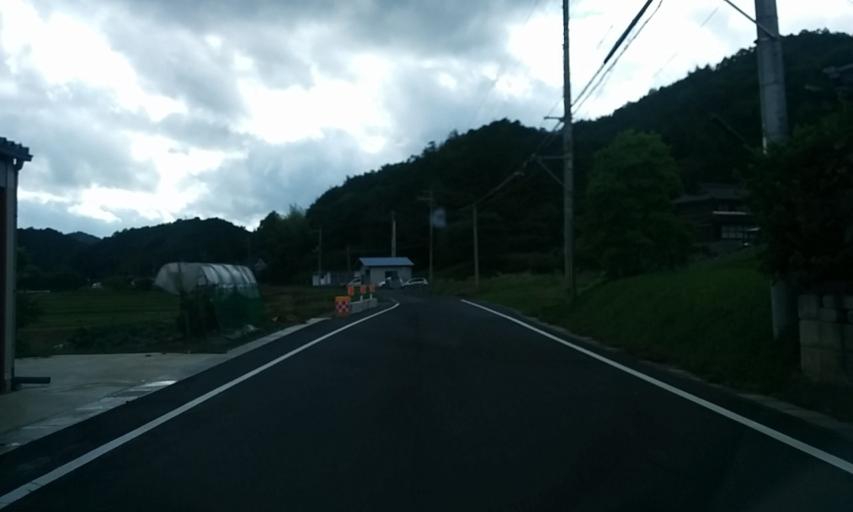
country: JP
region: Kyoto
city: Ayabe
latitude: 35.3766
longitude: 135.2329
